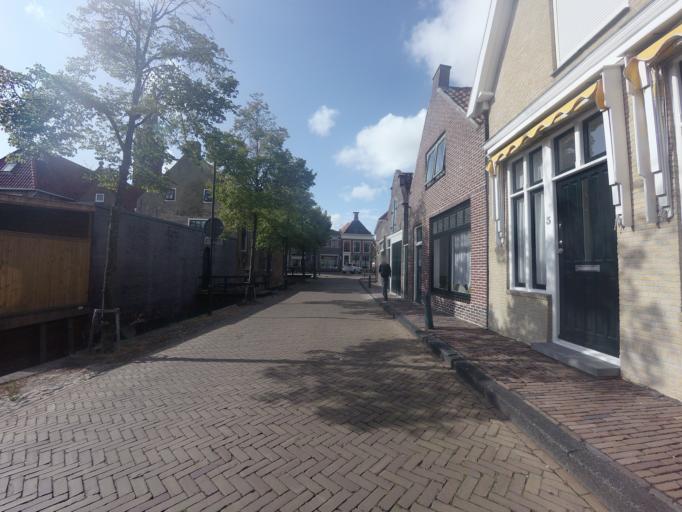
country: NL
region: Friesland
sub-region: Sudwest Fryslan
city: Bolsward
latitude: 53.0632
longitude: 5.5242
